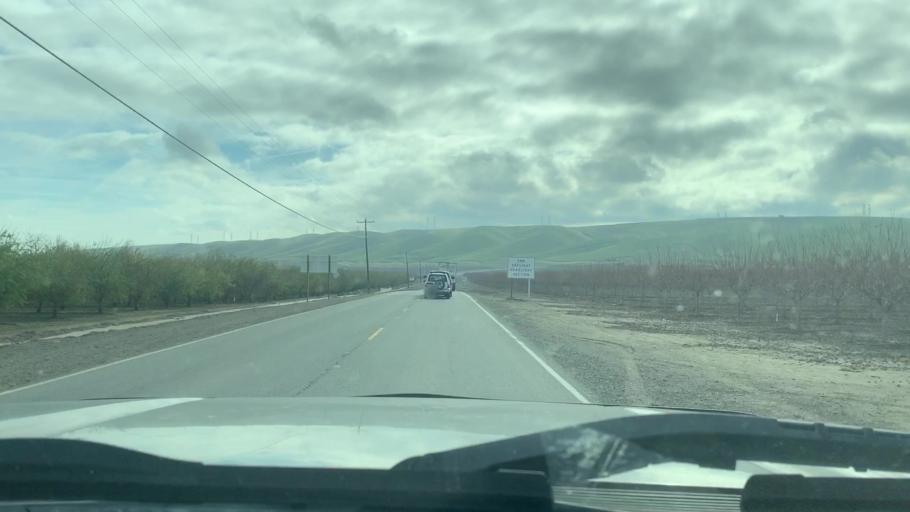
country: US
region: California
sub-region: Merced County
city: Los Banos
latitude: 36.9404
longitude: -120.8379
